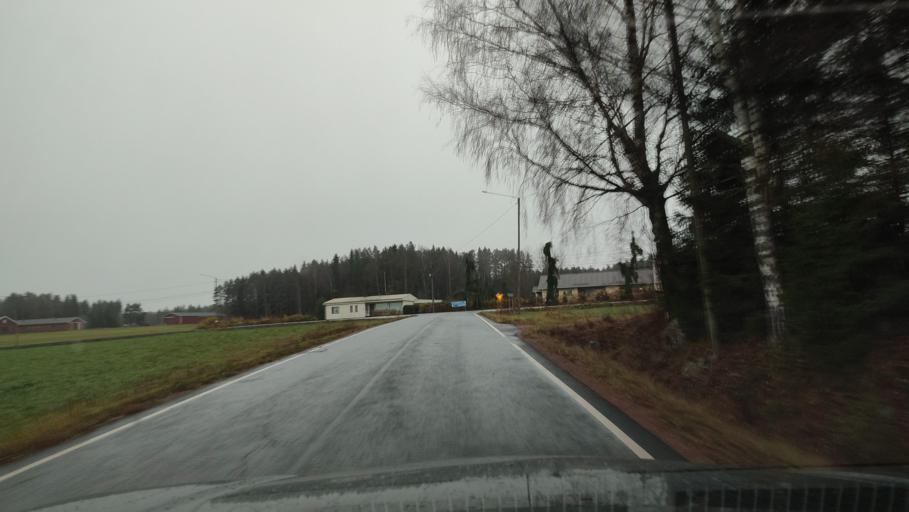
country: FI
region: Southern Ostrobothnia
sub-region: Suupohja
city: Karijoki
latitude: 62.1327
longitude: 21.6776
